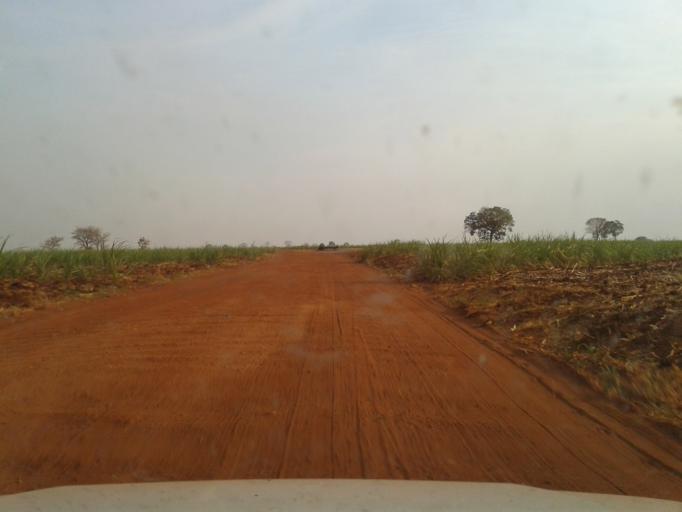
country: BR
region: Minas Gerais
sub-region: Capinopolis
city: Capinopolis
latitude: -18.7474
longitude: -49.6931
